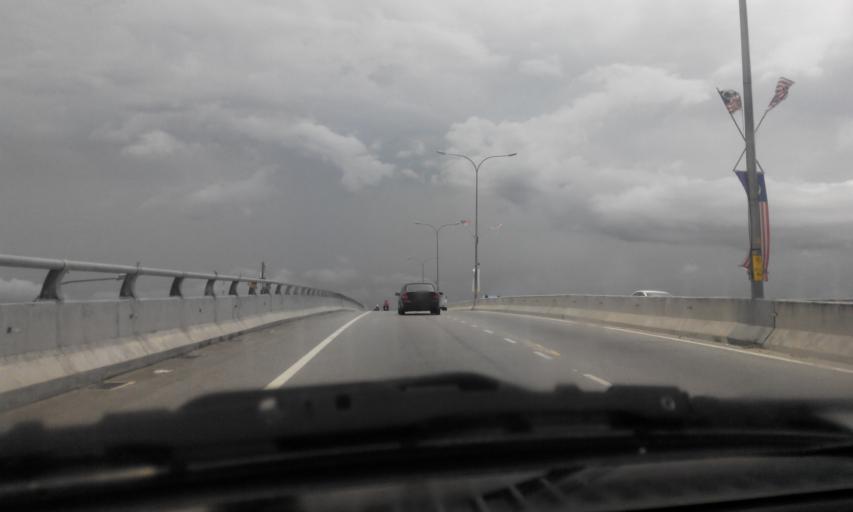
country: MY
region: Perak
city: Parit Buntar
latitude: 5.1221
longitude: 100.4872
